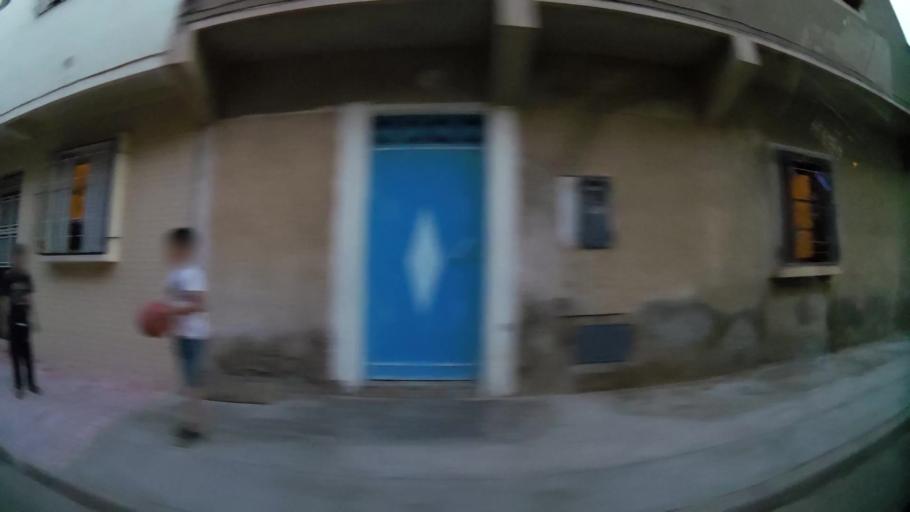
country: MA
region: Oriental
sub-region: Oujda-Angad
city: Oujda
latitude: 34.6850
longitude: -1.8751
